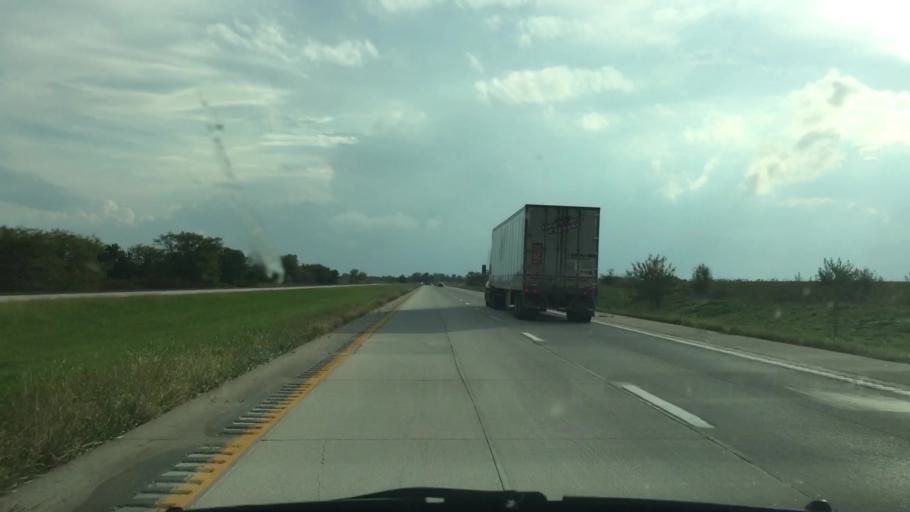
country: US
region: Missouri
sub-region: Daviess County
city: Gallatin
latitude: 39.9590
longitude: -94.1045
